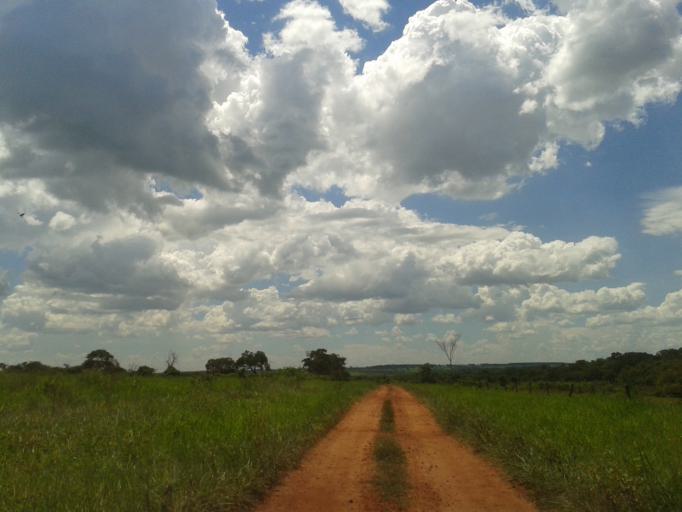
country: BR
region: Minas Gerais
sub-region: Santa Vitoria
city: Santa Vitoria
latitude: -19.1132
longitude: -50.5198
